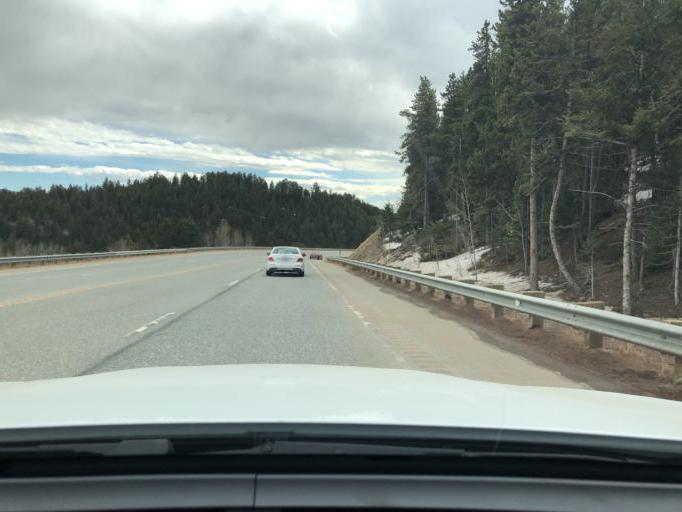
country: US
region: Colorado
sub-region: Gilpin County
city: Central City
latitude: 39.7854
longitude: -105.4849
